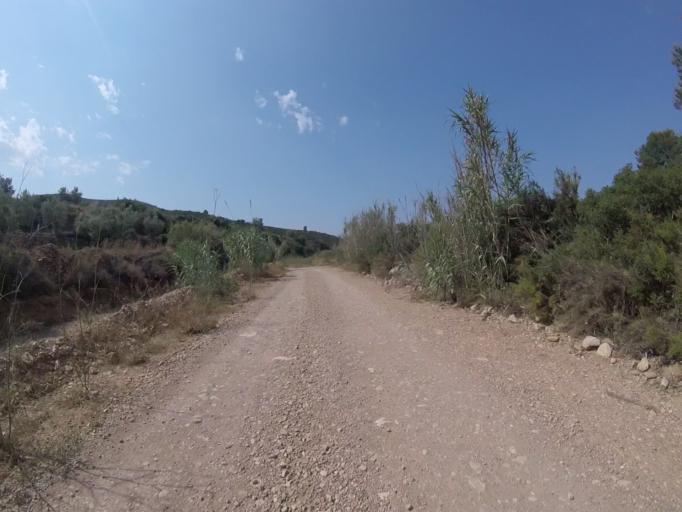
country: ES
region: Valencia
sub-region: Provincia de Castello
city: Cuevas de Vinroma
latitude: 40.3066
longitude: 0.1704
